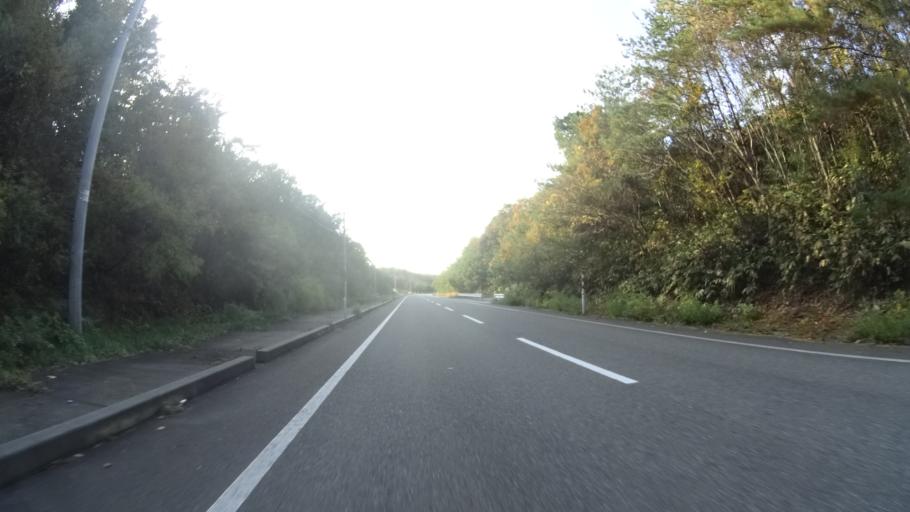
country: JP
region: Ishikawa
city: Hakui
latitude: 37.0710
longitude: 136.7401
